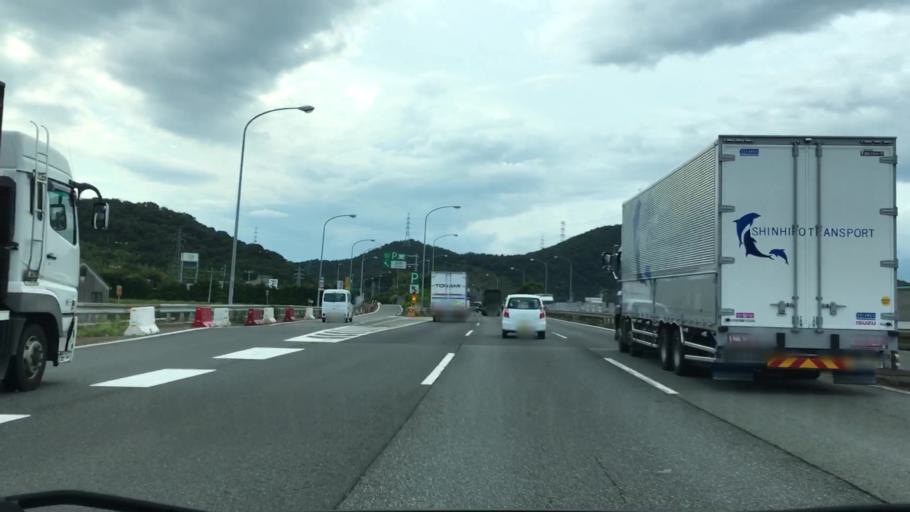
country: JP
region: Hyogo
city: Shirahamacho-usazakiminami
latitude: 34.7995
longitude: 134.7552
